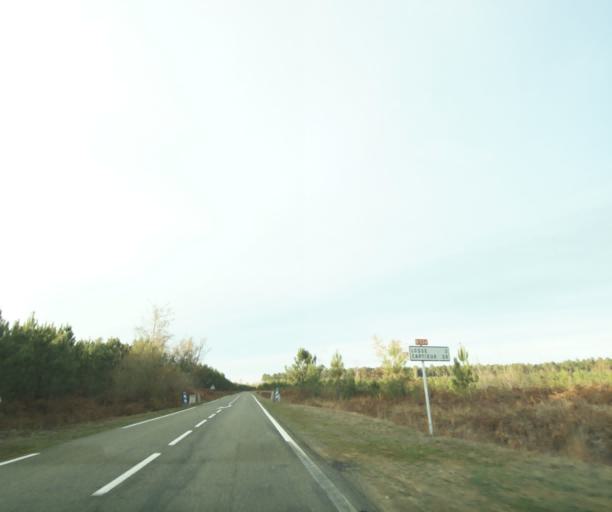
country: FR
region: Aquitaine
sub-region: Departement des Landes
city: Gabarret
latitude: 44.0871
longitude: -0.0940
